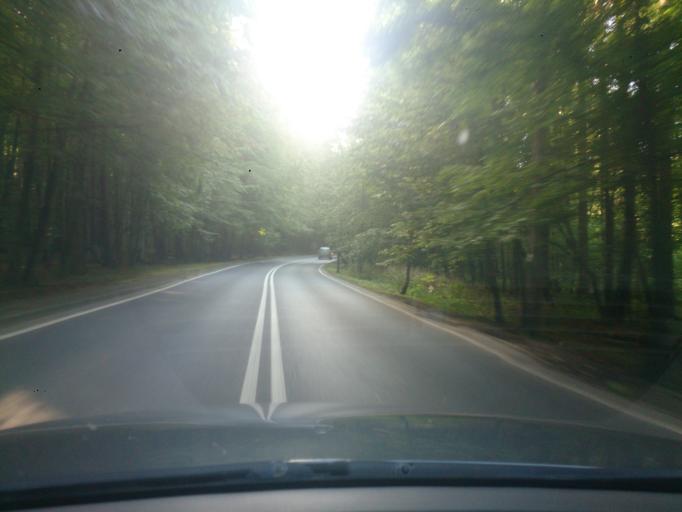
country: PL
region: Pomeranian Voivodeship
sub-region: Sopot
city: Sopot
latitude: 54.4560
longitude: 18.5261
